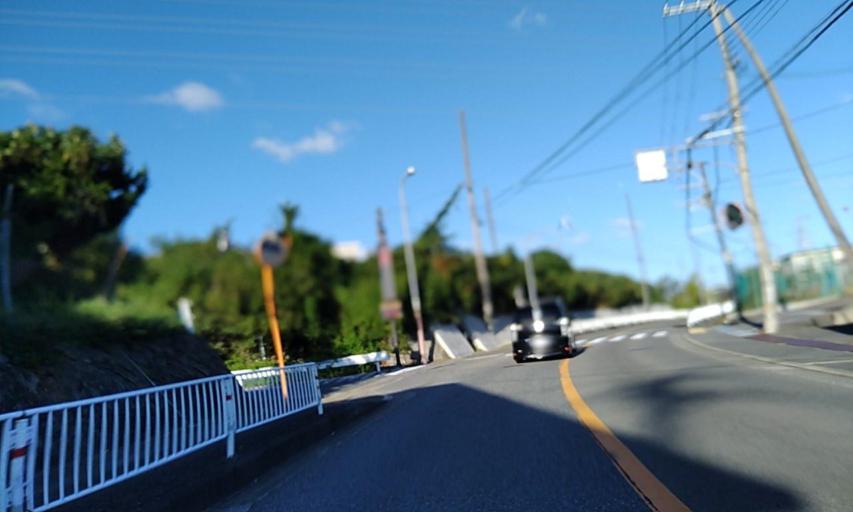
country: JP
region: Wakayama
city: Wakayama-shi
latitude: 34.3152
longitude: 135.1308
